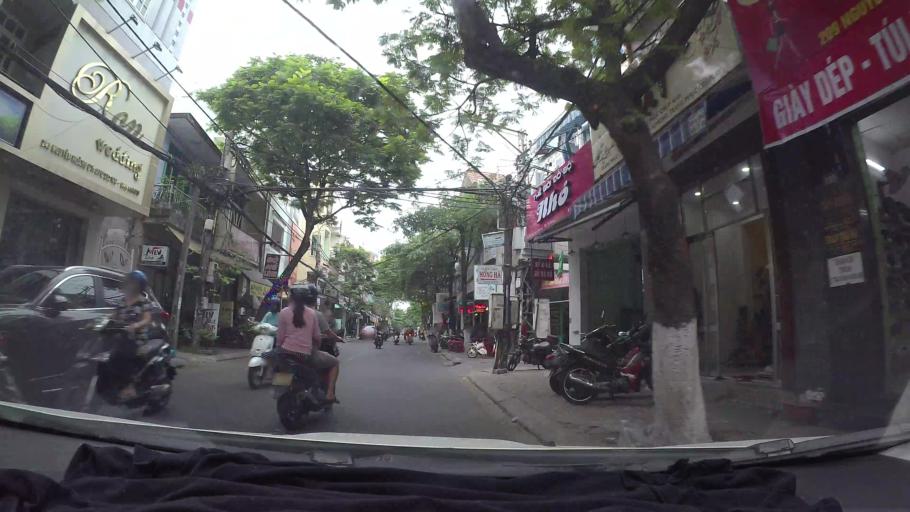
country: VN
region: Da Nang
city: Da Nang
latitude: 16.0588
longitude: 108.2133
